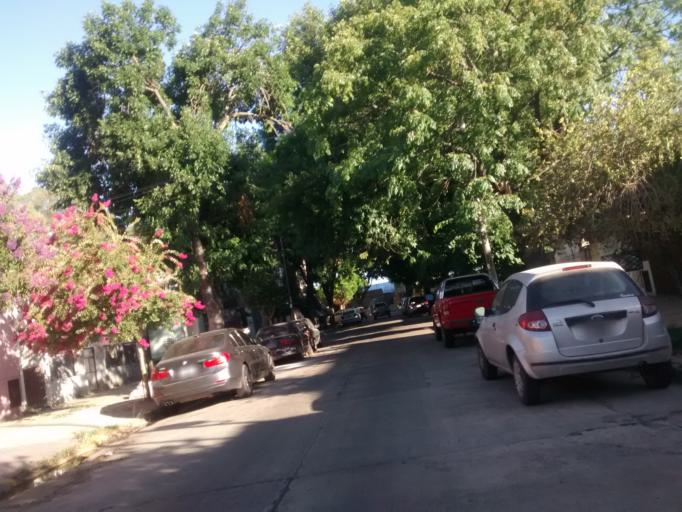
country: AR
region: Buenos Aires
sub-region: Partido de La Plata
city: La Plata
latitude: -34.9381
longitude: -57.9391
